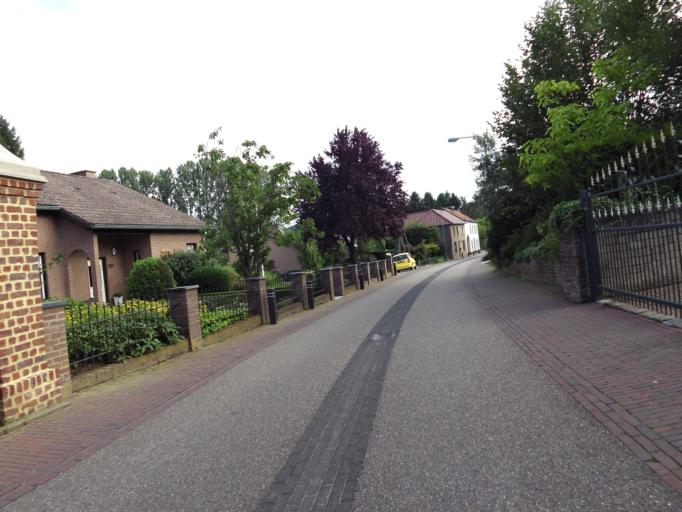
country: NL
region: Limburg
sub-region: Gemeente Schinnen
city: Schinnen
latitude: 50.9341
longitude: 5.8934
